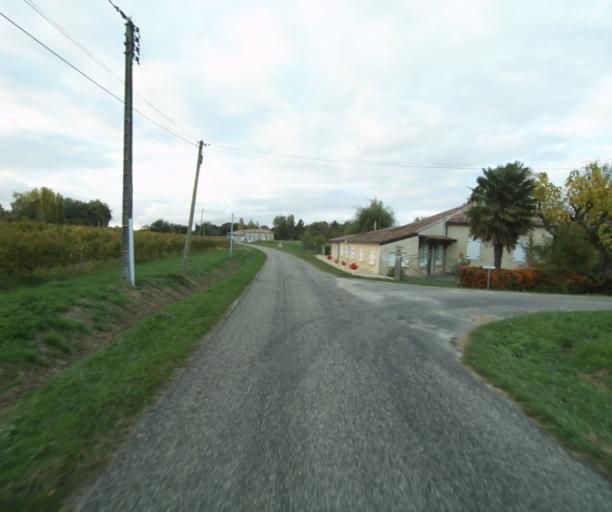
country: FR
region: Aquitaine
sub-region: Departement des Landes
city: Gabarret
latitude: 43.9777
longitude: 0.0930
